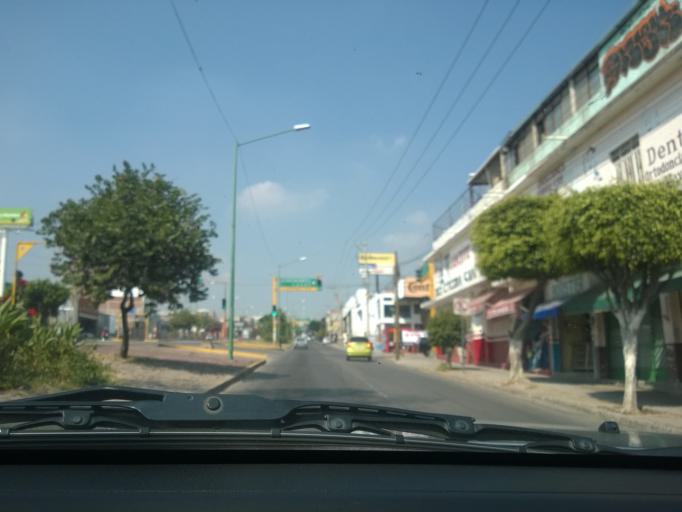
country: MX
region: Guanajuato
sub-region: Leon
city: La Ermita
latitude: 21.1320
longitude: -101.7089
